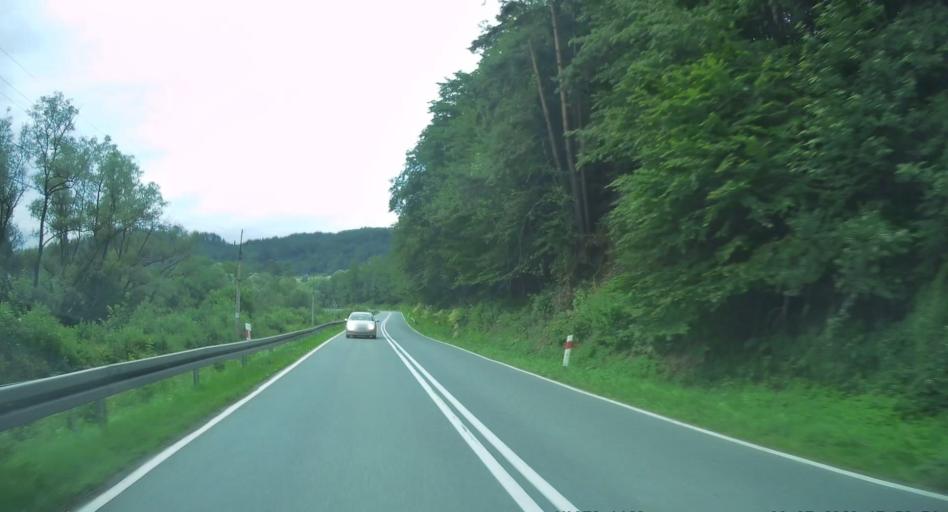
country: PL
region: Lesser Poland Voivodeship
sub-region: Powiat nowosadecki
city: Piwniczna-Zdroj
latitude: 49.3808
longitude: 20.7615
